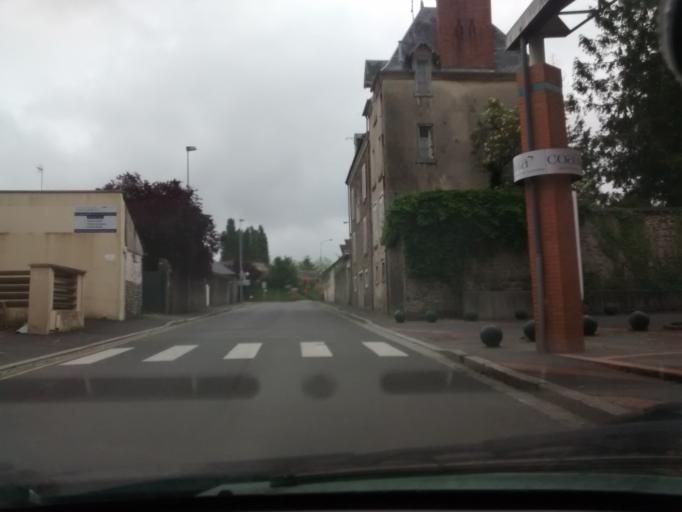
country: FR
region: Lower Normandy
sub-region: Departement de la Manche
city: Saint-Lo
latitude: 49.1110
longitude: -1.0916
